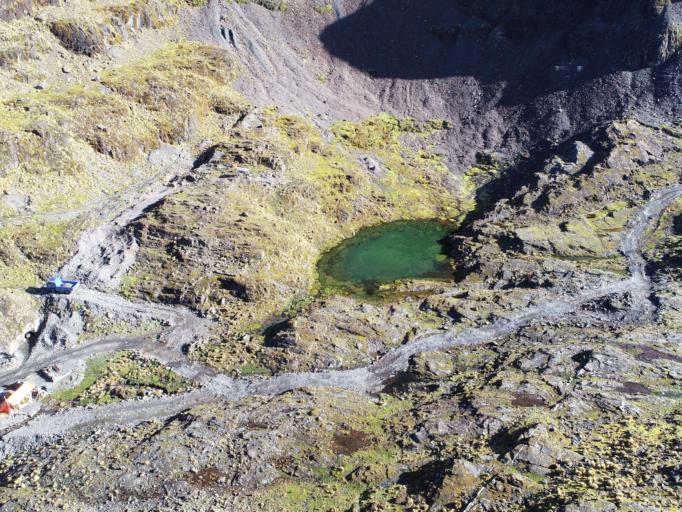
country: PE
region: Puno
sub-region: San Antonio De Putina
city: Sina
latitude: -14.7411
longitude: -69.0519
